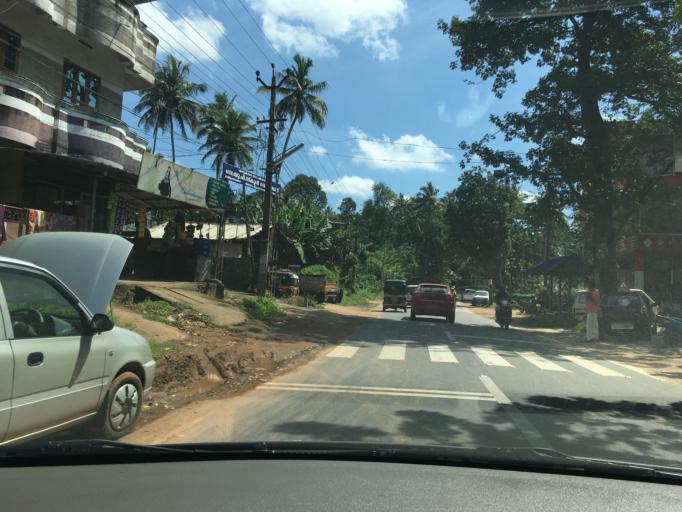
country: IN
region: Kerala
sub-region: Thiruvananthapuram
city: Nedumangad
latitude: 8.5787
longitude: 76.9964
